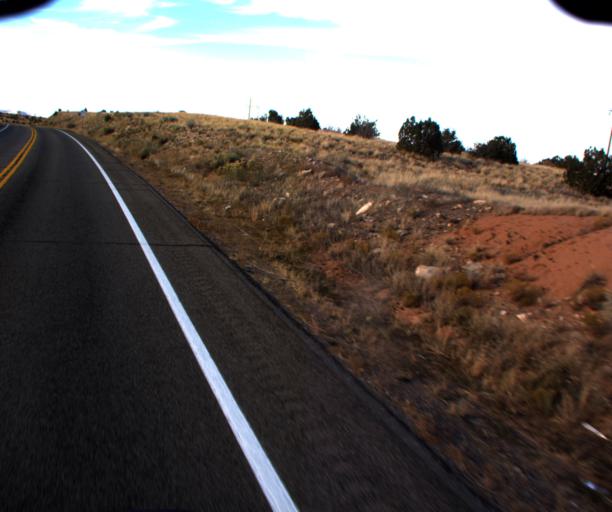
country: US
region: New Mexico
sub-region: San Juan County
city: Shiprock
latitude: 36.8790
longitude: -109.0481
